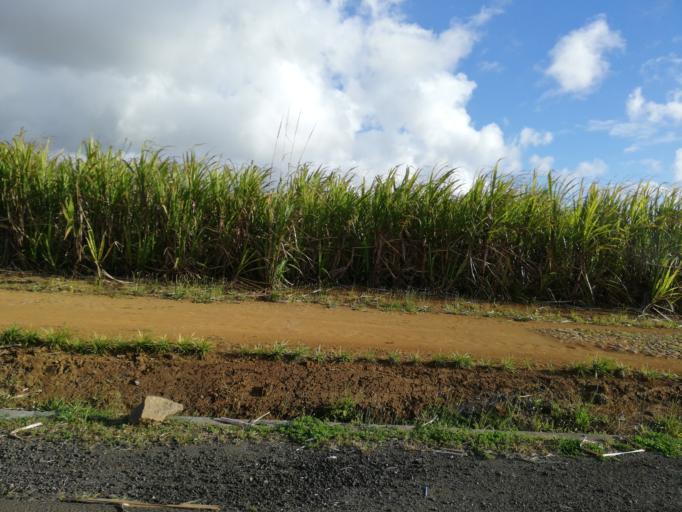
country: MU
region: Moka
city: La Dagotiere
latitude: -20.2345
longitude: 57.5689
